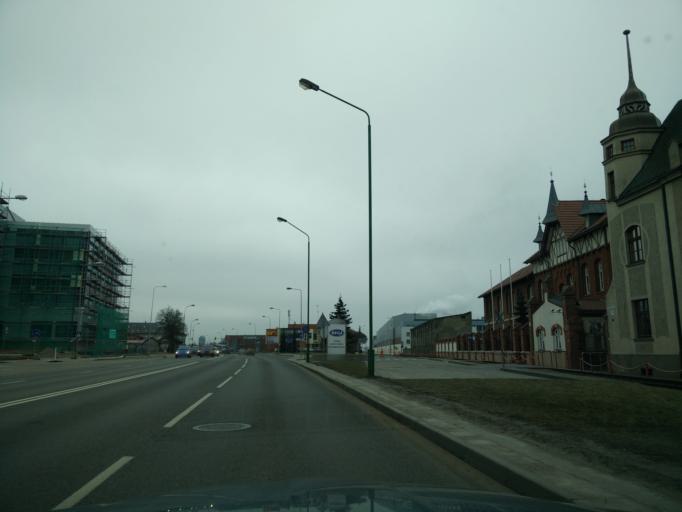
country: LT
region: Klaipedos apskritis
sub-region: Klaipeda
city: Klaipeda
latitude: 55.6985
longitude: 21.1367
